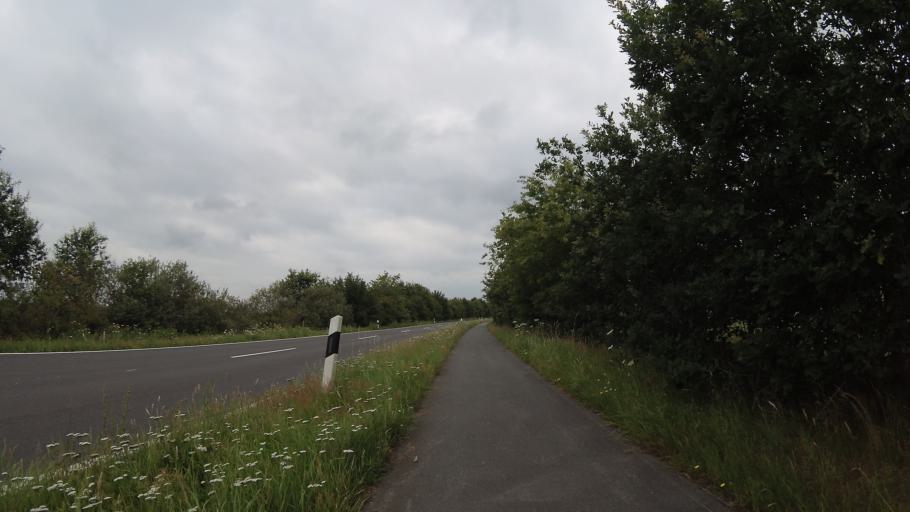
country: DE
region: Lower Saxony
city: Oberlangen
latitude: 52.8369
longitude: 7.2550
